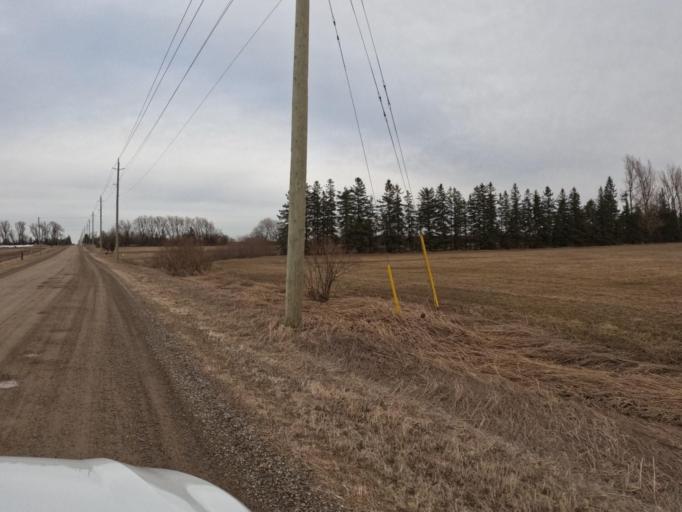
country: CA
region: Ontario
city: Orangeville
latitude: 43.9195
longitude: -80.2265
